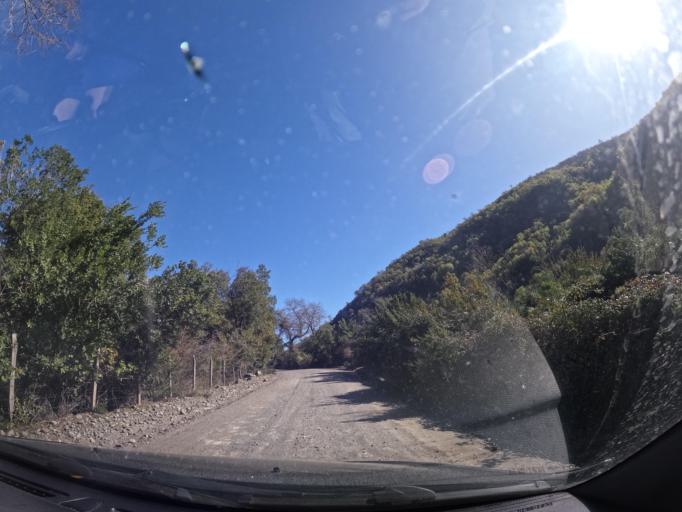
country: CL
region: Maule
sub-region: Provincia de Linares
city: Longavi
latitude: -36.2283
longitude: -71.3961
